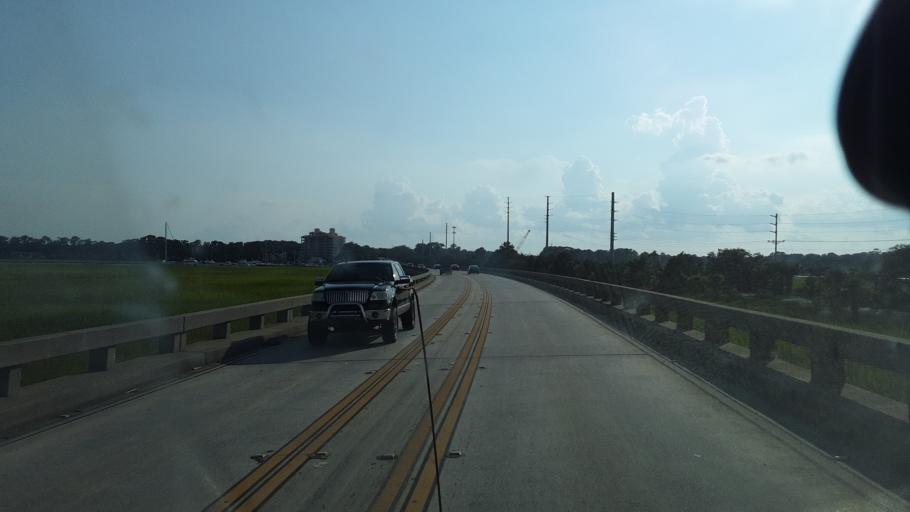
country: US
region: Georgia
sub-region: Chatham County
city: Wilmington Island
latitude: 32.0395
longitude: -80.9545
